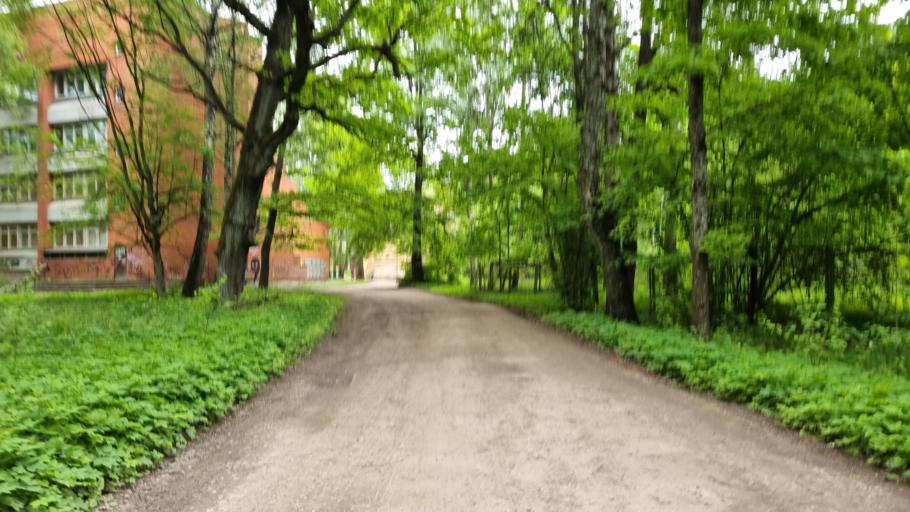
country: LV
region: Marupe
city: Marupe
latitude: 56.9517
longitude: 24.0142
